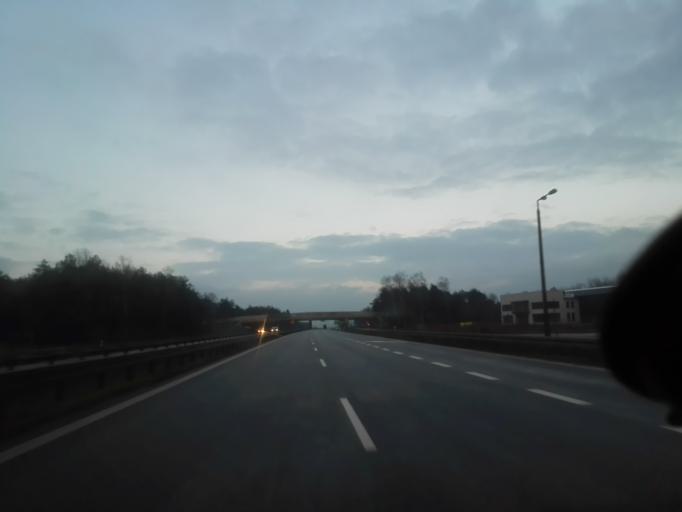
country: PL
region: Masovian Voivodeship
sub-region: Powiat wolominski
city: Dabrowka
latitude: 52.4421
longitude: 21.2472
